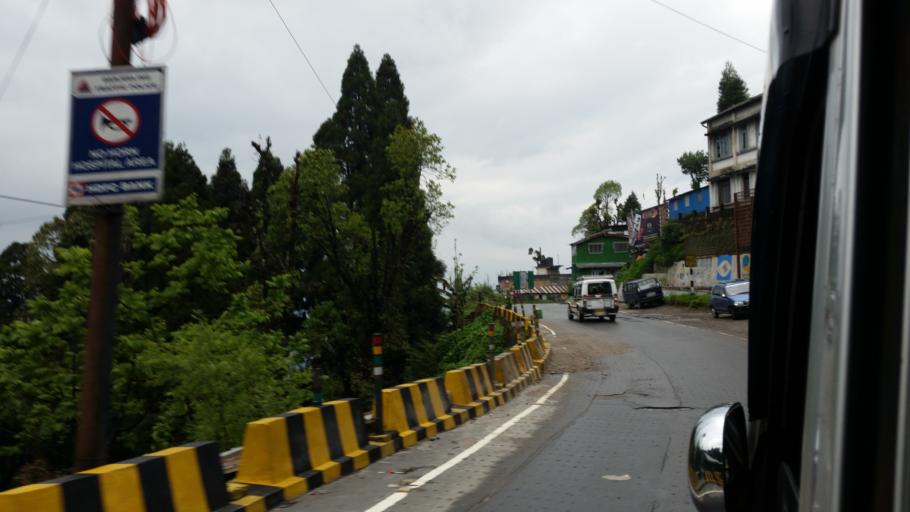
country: IN
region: West Bengal
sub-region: Darjiling
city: Darjiling
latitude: 27.0192
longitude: 88.2502
